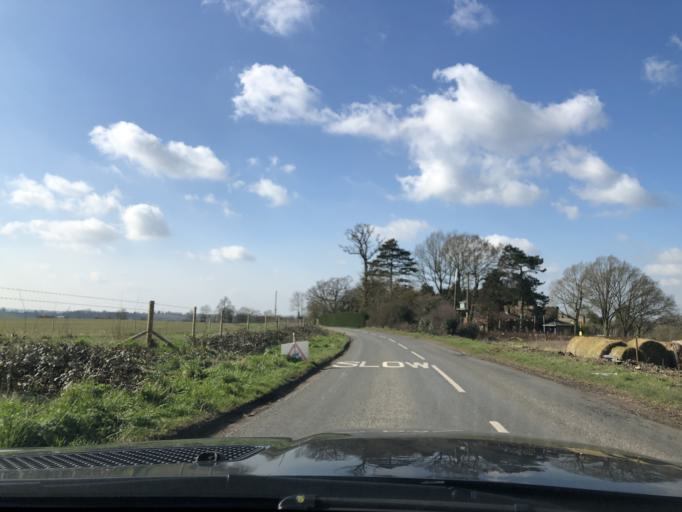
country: GB
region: England
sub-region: Warwickshire
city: Harbury
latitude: 52.2873
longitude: -1.4593
